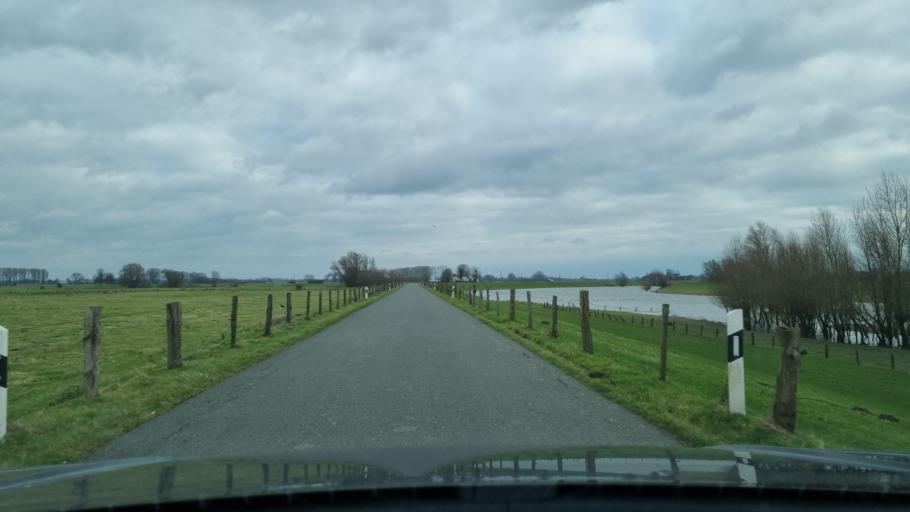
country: DE
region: North Rhine-Westphalia
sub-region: Regierungsbezirk Dusseldorf
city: Kleve
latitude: 51.8332
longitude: 6.1224
